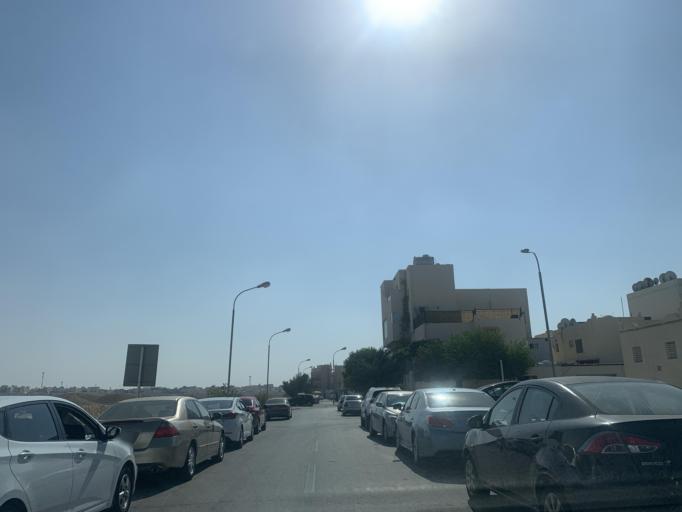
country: BH
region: Central Governorate
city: Madinat Hamad
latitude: 26.1241
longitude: 50.4965
